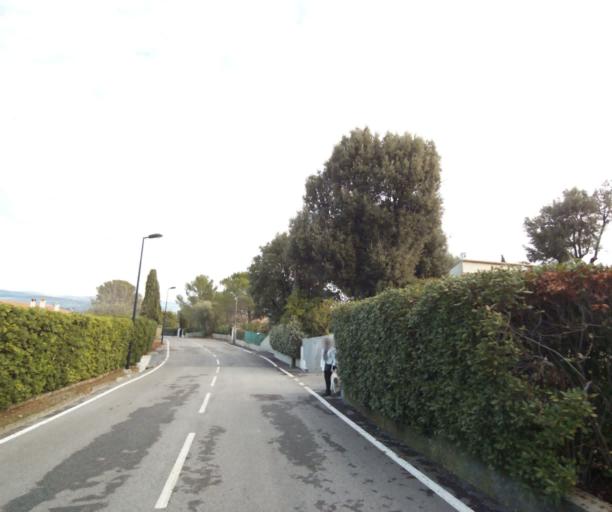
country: FR
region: Provence-Alpes-Cote d'Azur
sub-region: Departement du Var
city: Trans-en-Provence
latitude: 43.4899
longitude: 6.4968
